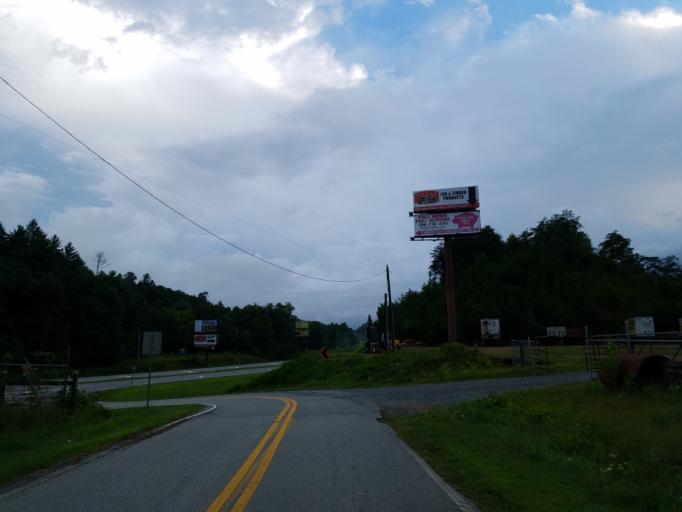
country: US
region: Georgia
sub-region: Fannin County
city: Blue Ridge
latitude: 34.8359
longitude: -84.3476
